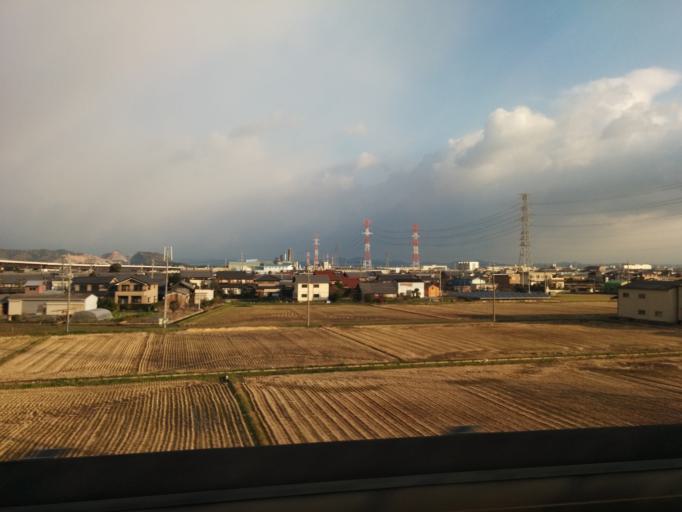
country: JP
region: Gifu
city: Ogaki
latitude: 35.3490
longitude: 136.5811
